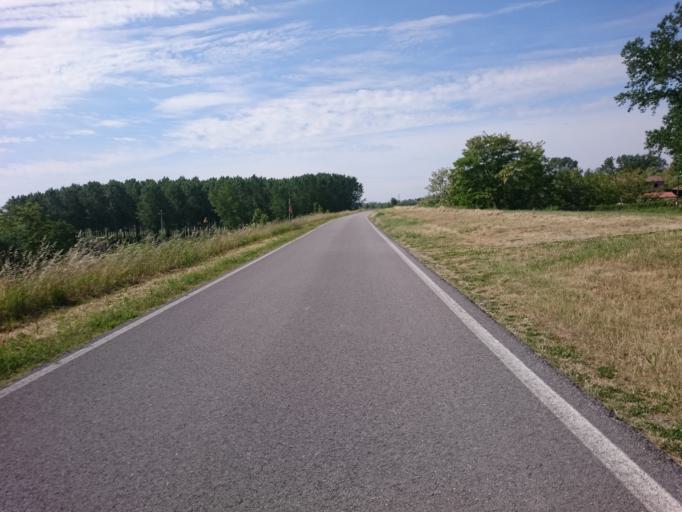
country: IT
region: Veneto
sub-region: Provincia di Rovigo
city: Corbola
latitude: 44.9824
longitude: 12.0859
